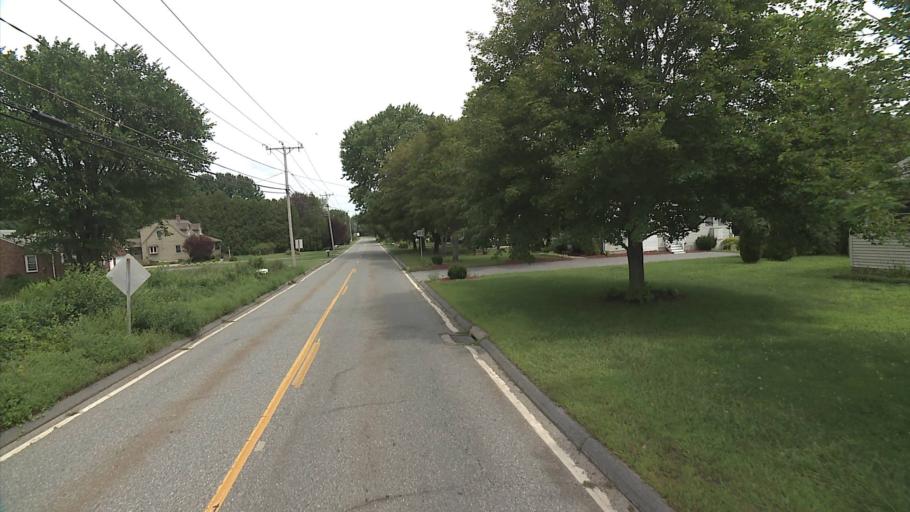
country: US
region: Connecticut
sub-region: Windham County
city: Thompson
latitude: 42.0044
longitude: -71.8453
